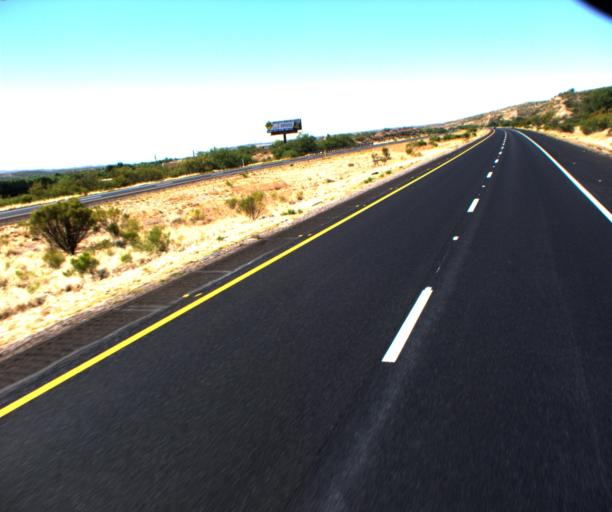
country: US
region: Arizona
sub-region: Santa Cruz County
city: Tubac
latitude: 31.5852
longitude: -111.0549
